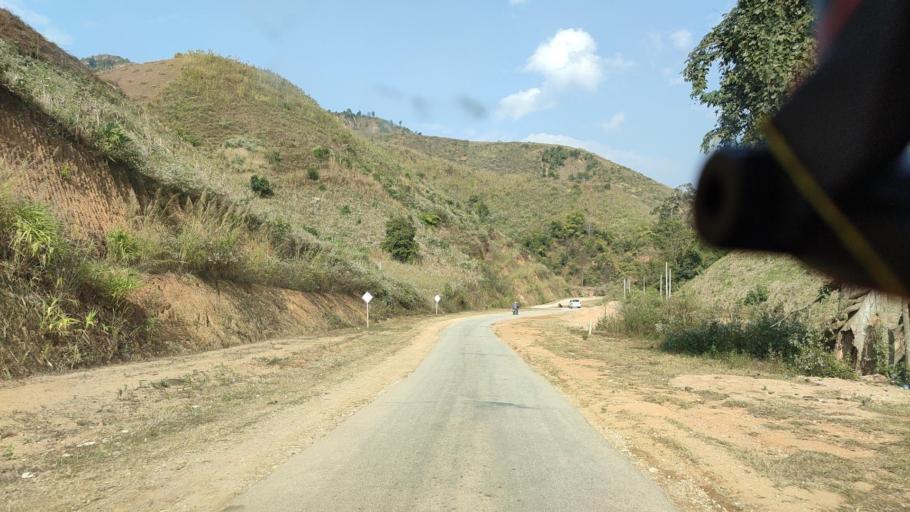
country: CN
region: Yunnan
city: Nayun
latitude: 21.7879
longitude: 99.5179
